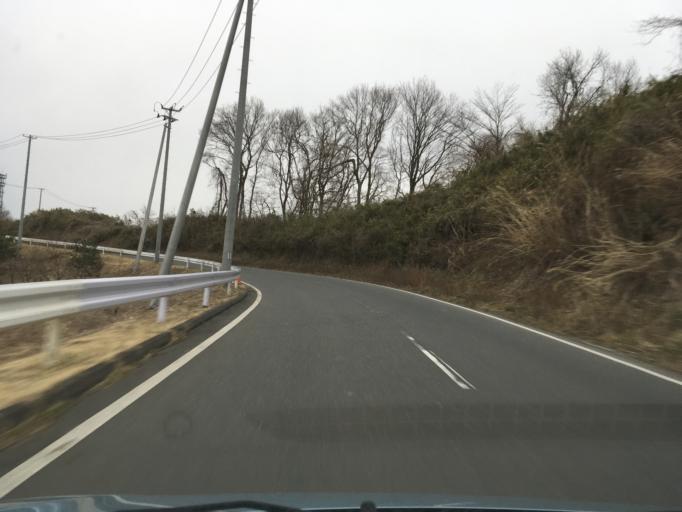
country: JP
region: Miyagi
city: Wakuya
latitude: 38.6982
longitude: 141.1687
